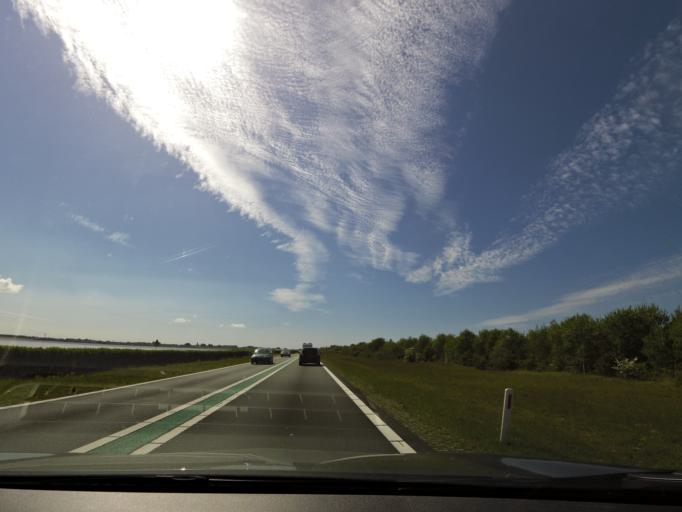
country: NL
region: Zeeland
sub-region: Schouwen-Duiveland
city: Bruinisse
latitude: 51.6753
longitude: 4.1197
